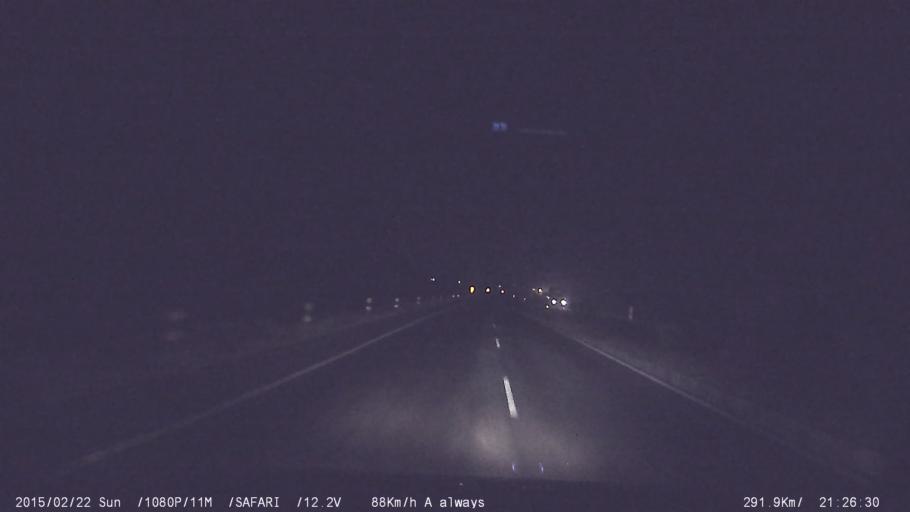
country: IN
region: Tamil Nadu
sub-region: Karur
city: Karur
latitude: 10.9059
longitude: 78.0365
